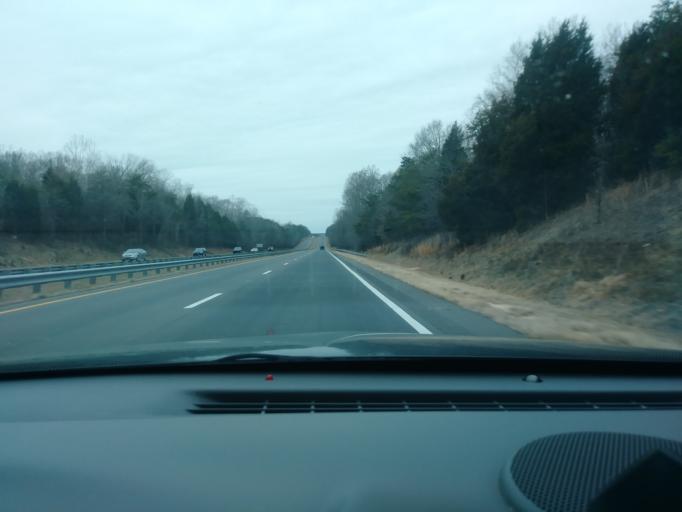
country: US
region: North Carolina
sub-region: Forsyth County
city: Lewisville
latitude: 36.1018
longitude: -80.4770
